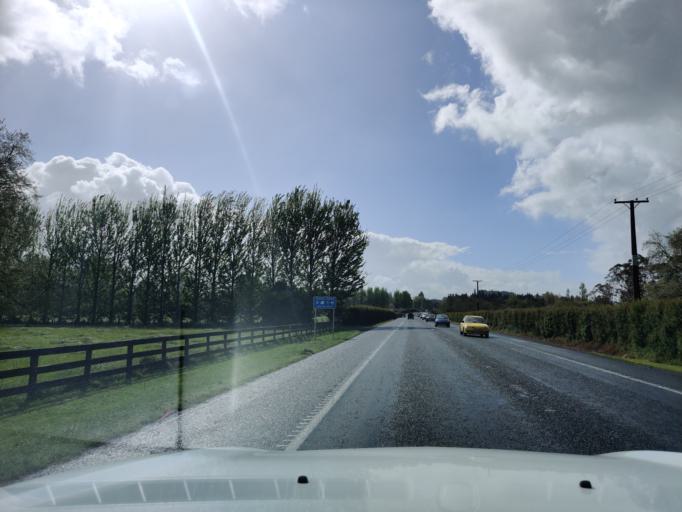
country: NZ
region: Waikato
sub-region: Waipa District
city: Cambridge
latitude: -37.9141
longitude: 175.5453
